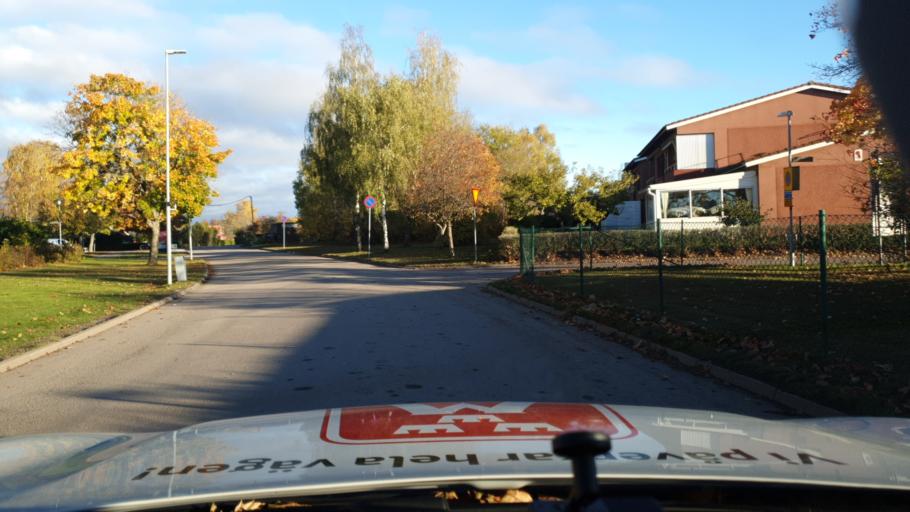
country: SE
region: Vaestmanland
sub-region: Vasteras
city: Vasteras
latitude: 59.6439
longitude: 16.5387
